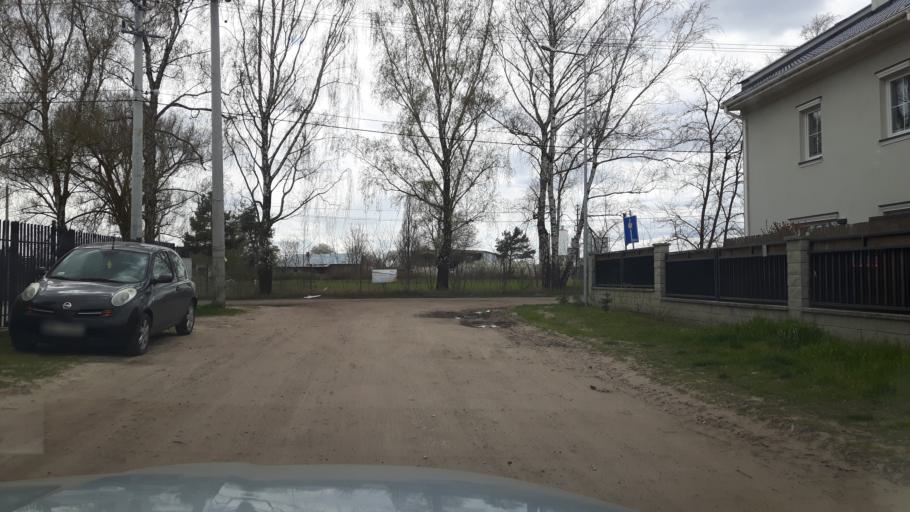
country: PL
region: Masovian Voivodeship
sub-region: Powiat wolominski
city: Kobylka
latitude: 52.3448
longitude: 21.1913
